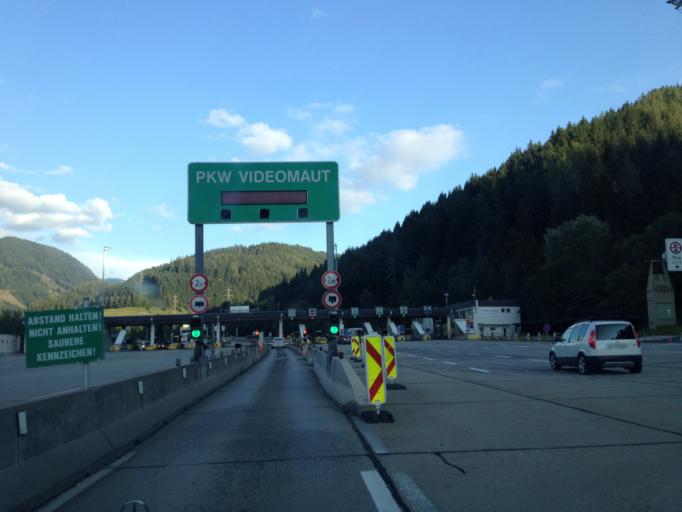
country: AT
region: Styria
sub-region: Politischer Bezirk Leoben
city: Sankt Michael in Obersteiermark
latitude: 47.3243
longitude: 15.0288
